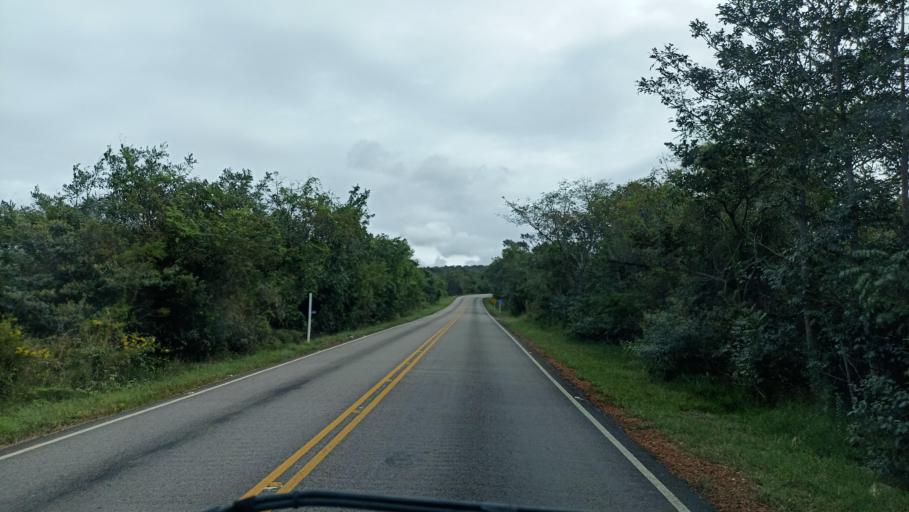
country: BR
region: Bahia
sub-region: Andarai
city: Vera Cruz
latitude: -12.9302
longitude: -41.2361
